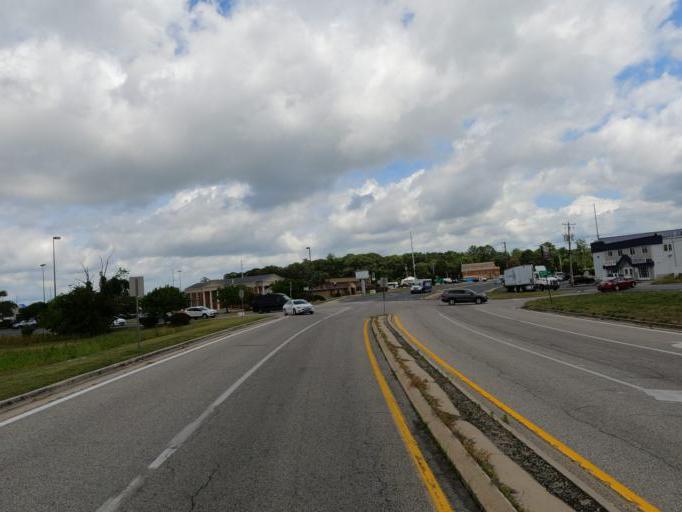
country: US
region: Delaware
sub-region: Sussex County
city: Lewes
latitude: 38.7264
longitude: -75.1304
